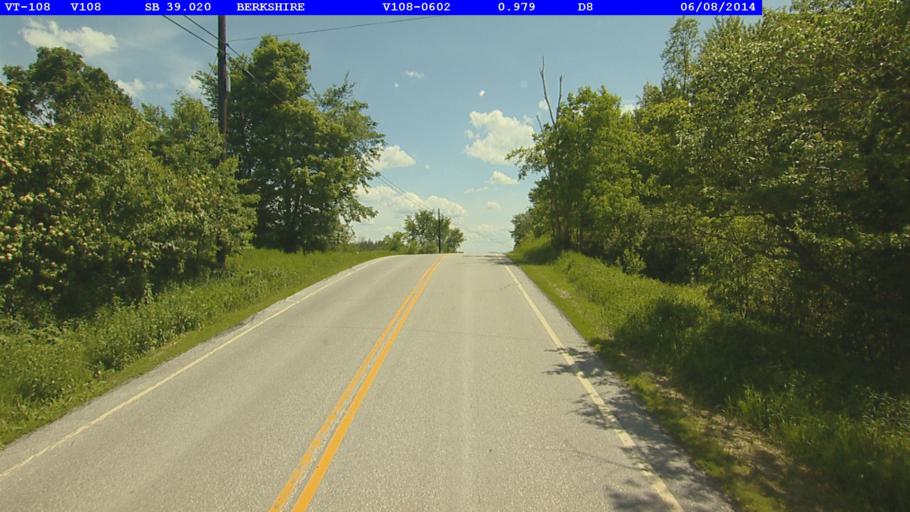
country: US
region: Vermont
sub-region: Franklin County
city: Enosburg Falls
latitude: 44.9388
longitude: -72.8125
